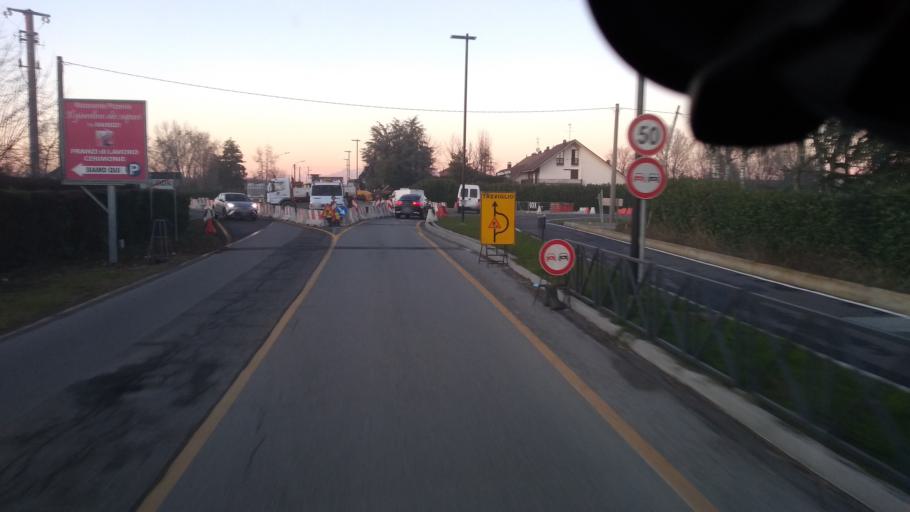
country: IT
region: Lombardy
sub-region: Provincia di Bergamo
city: Calvenzano
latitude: 45.5005
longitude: 9.5985
